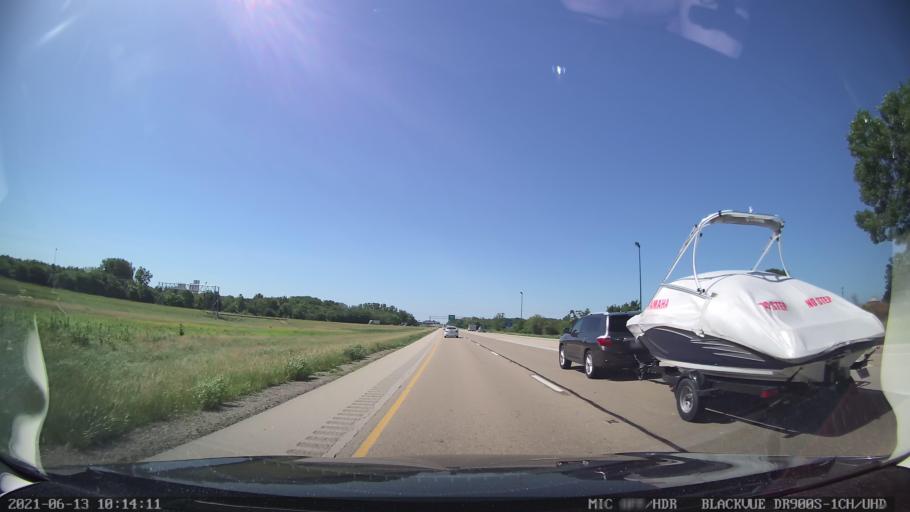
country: US
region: Illinois
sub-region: Logan County
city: Lincoln
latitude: 40.1740
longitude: -89.4181
